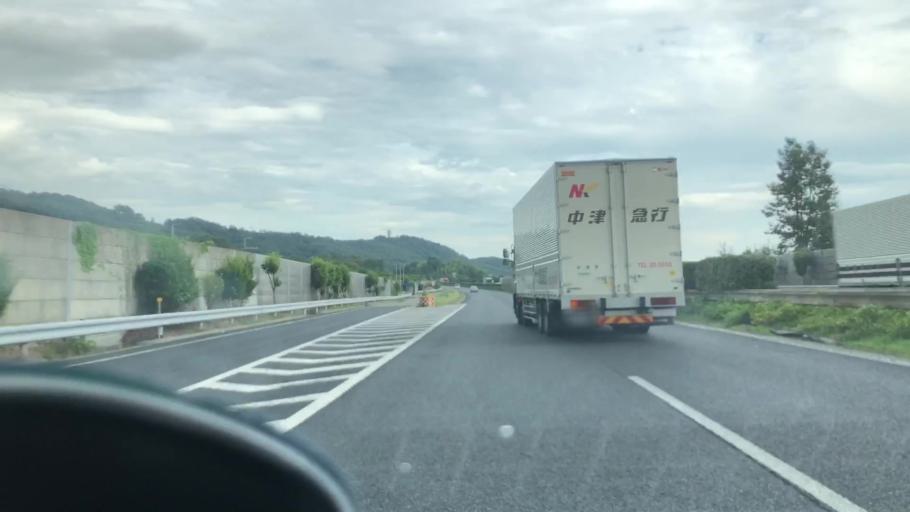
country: JP
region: Hyogo
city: Ono
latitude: 34.9360
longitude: 134.8353
